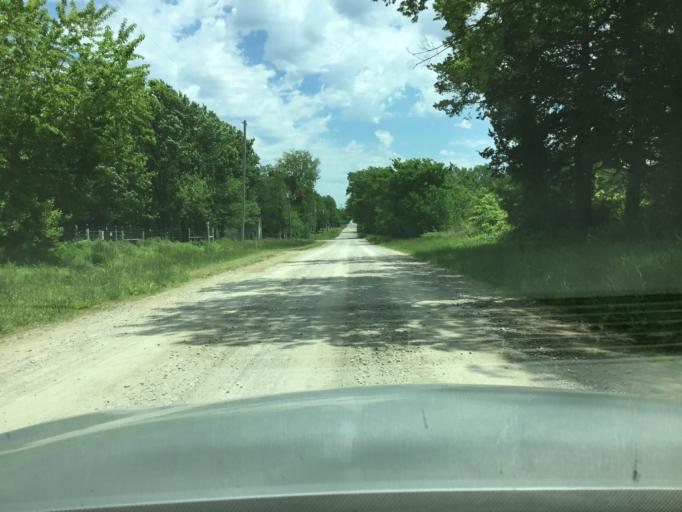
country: US
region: Kansas
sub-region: Montgomery County
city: Independence
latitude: 37.1095
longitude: -95.7664
